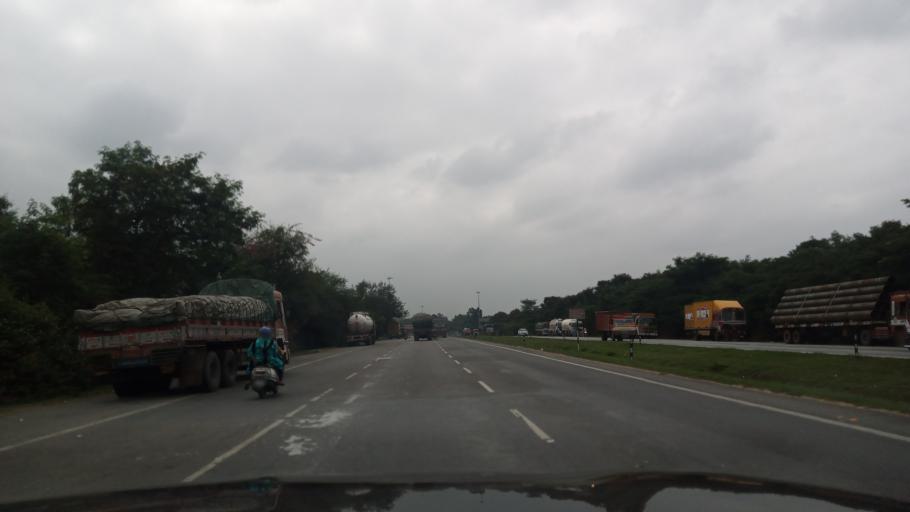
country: IN
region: Karnataka
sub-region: Bangalore Rural
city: Nelamangala
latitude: 13.0482
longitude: 77.4760
